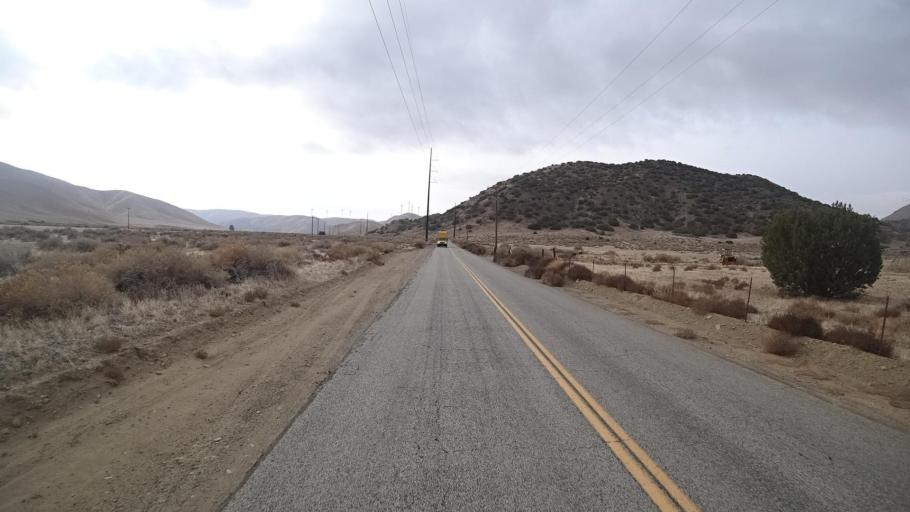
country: US
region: California
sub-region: Kern County
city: Tehachapi
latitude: 35.1330
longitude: -118.3251
